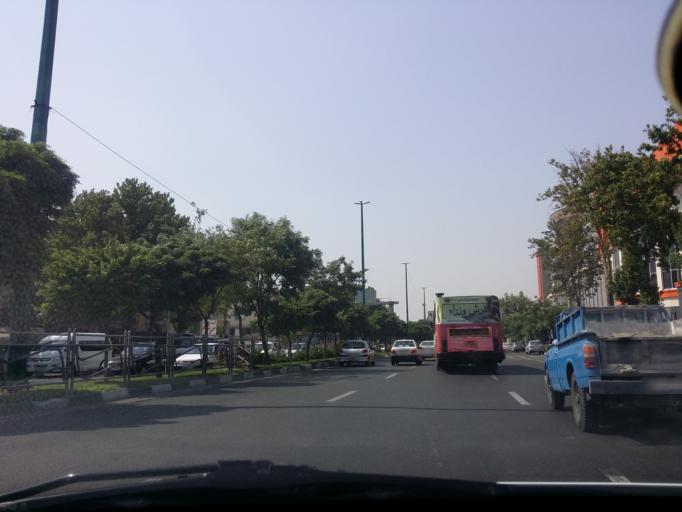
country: IR
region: Alborz
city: Karaj
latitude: 35.7948
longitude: 51.0023
